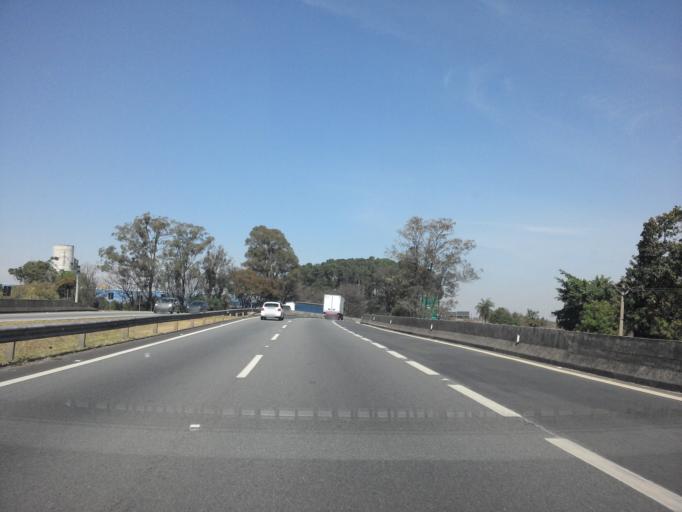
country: BR
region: Sao Paulo
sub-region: Campinas
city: Campinas
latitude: -22.8975
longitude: -47.1116
